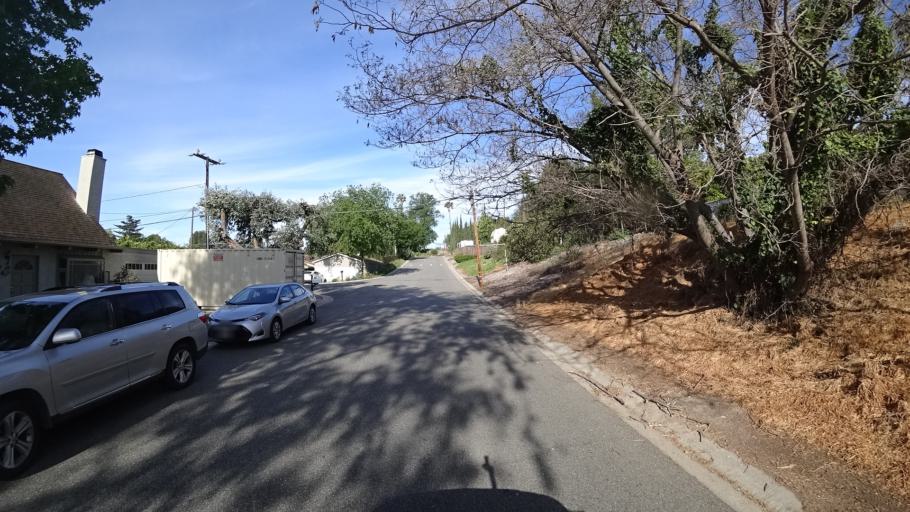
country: US
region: California
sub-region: Ventura County
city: Thousand Oaks
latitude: 34.1877
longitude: -118.8671
